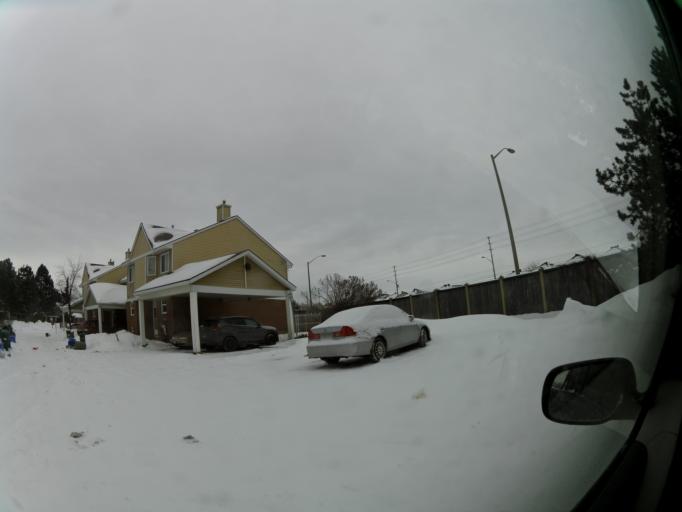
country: CA
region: Ontario
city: Ottawa
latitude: 45.3712
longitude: -75.6227
